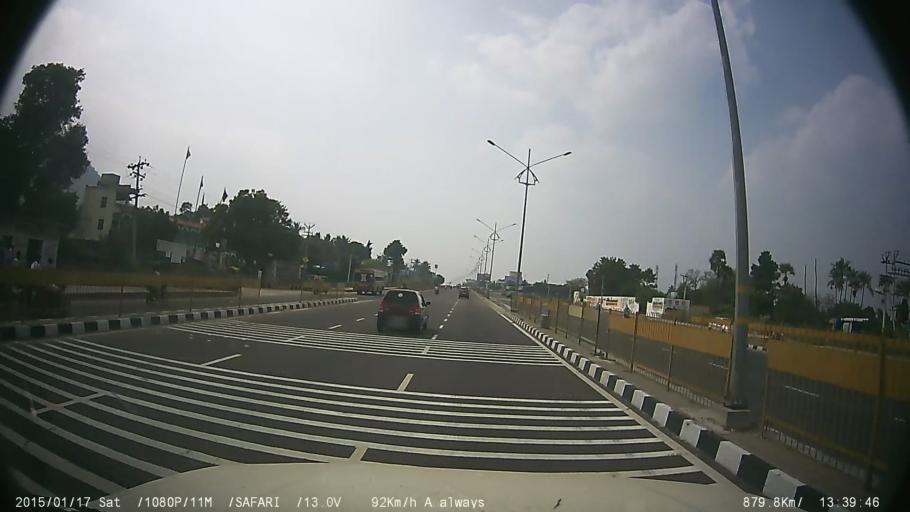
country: IN
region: Tamil Nadu
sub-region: Vellore
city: Katpadi
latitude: 12.9409
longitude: 79.1770
